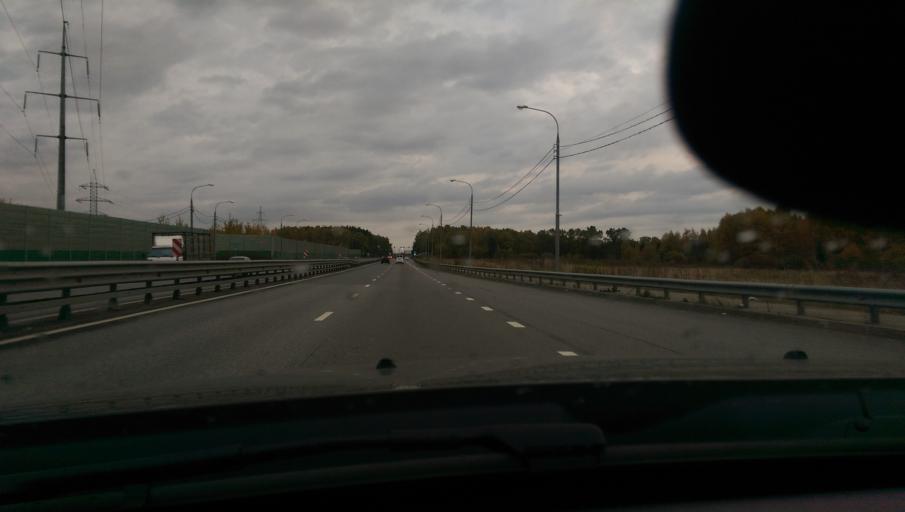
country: RU
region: Moscow
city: Vatutino
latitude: 55.9343
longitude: 37.6577
